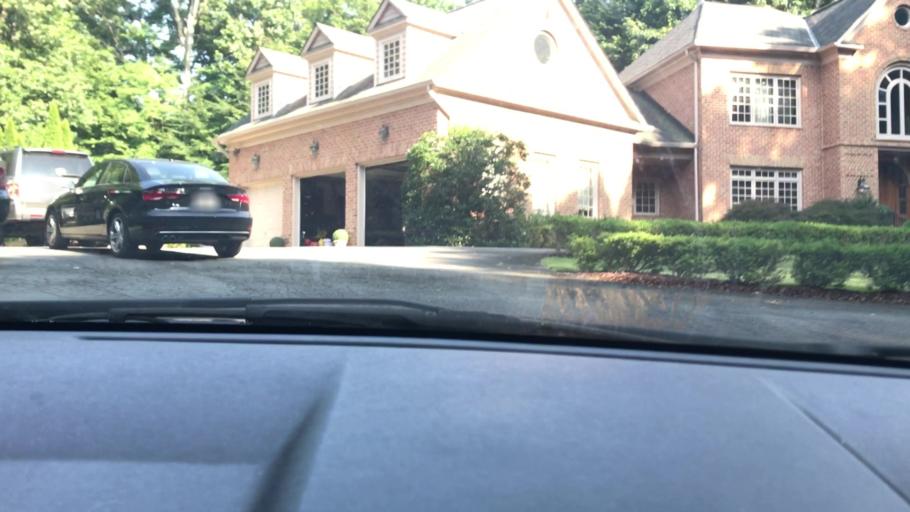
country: US
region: Virginia
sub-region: Fairfax County
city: Great Falls
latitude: 39.0109
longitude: -77.2662
